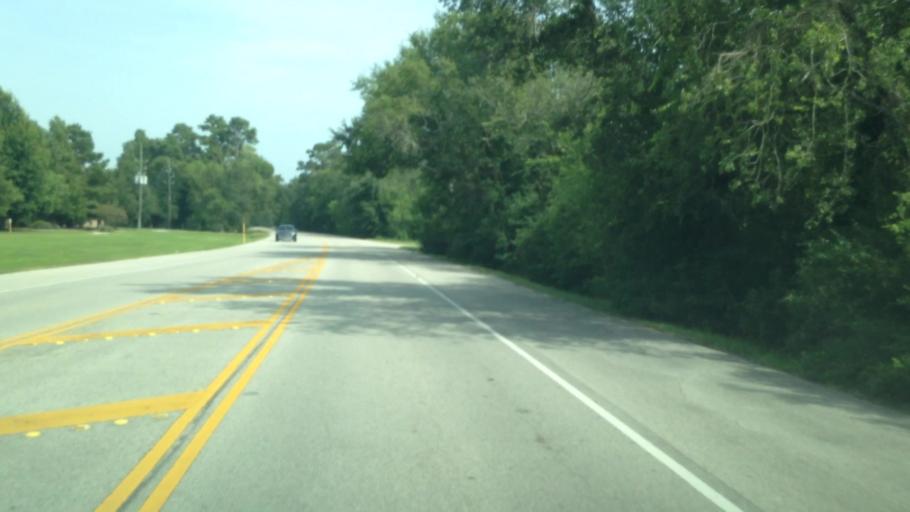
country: US
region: Texas
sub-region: Harris County
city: Atascocita
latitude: 29.9268
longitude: -95.1725
